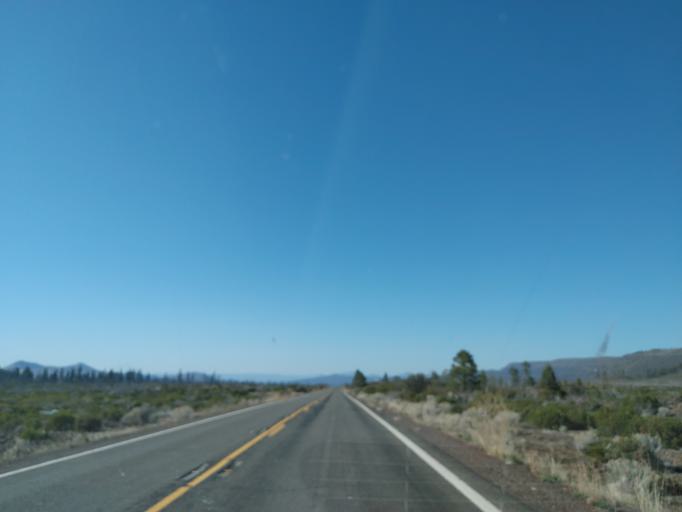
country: US
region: California
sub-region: Shasta County
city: Burney
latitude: 40.7060
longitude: -121.4189
